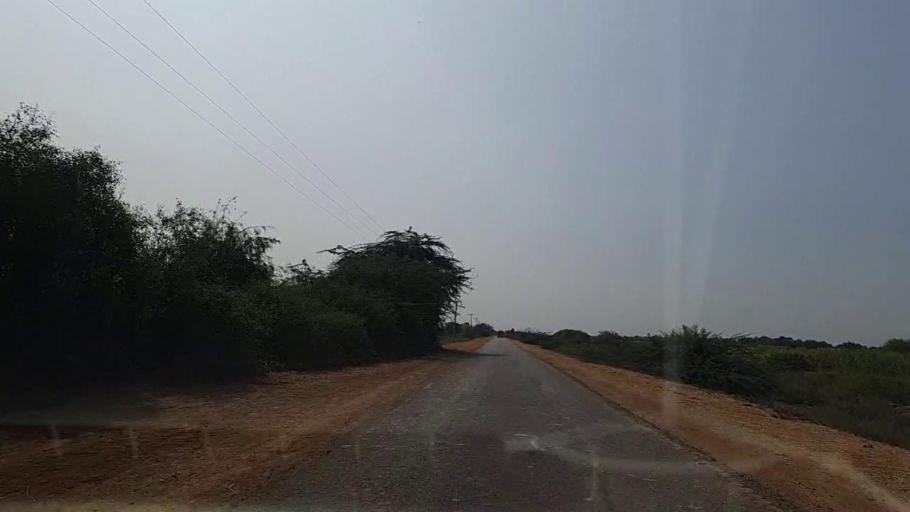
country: PK
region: Sindh
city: Chuhar Jamali
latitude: 24.3659
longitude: 67.9637
